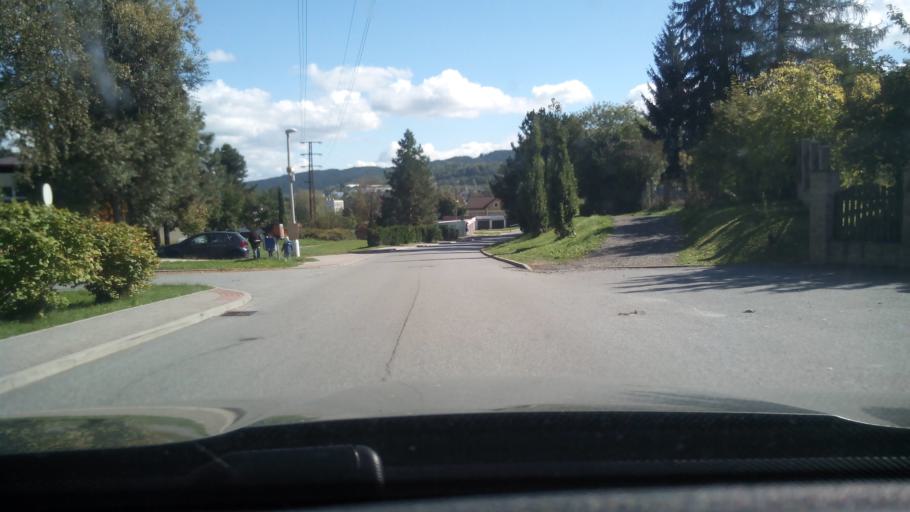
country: CZ
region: Jihocesky
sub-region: Okres Prachatice
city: Vimperk
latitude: 49.0587
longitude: 13.7757
